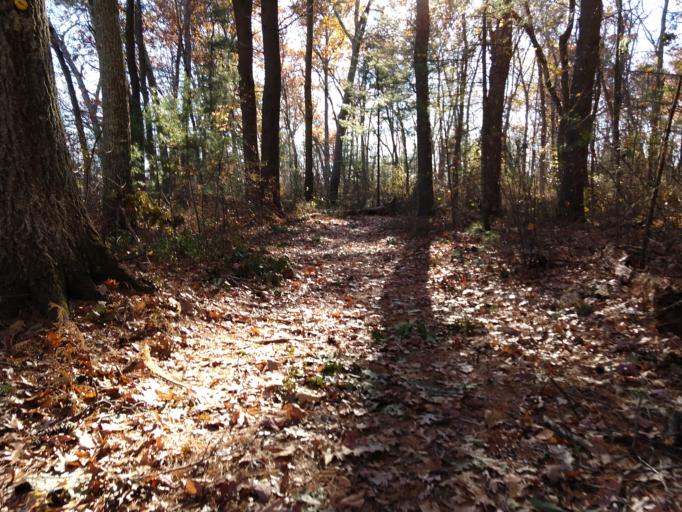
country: US
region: Massachusetts
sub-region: Middlesex County
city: Concord
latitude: 42.4839
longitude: -71.3270
